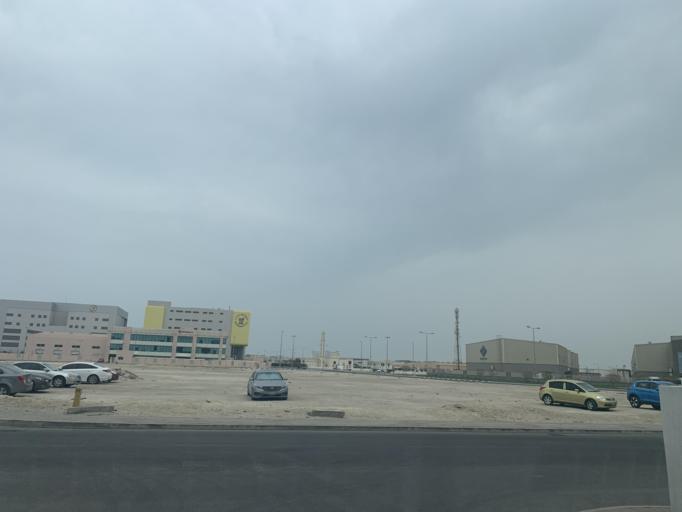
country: BH
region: Muharraq
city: Al Hadd
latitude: 26.2139
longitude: 50.6681
